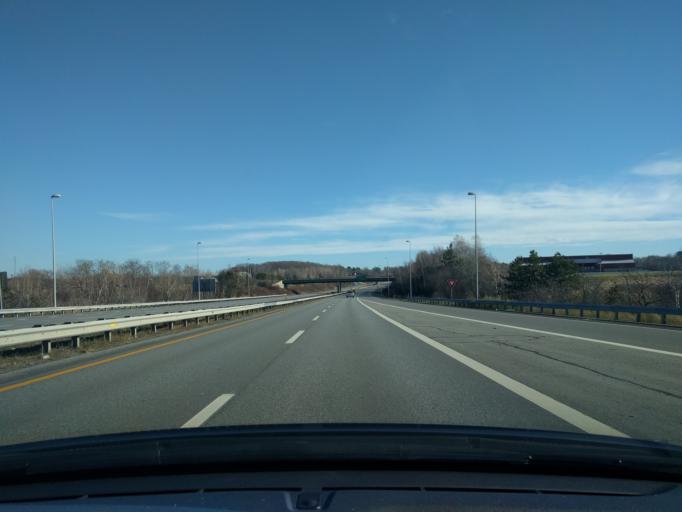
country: US
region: Maine
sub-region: Penobscot County
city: Brewer
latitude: 44.7832
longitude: -68.7687
